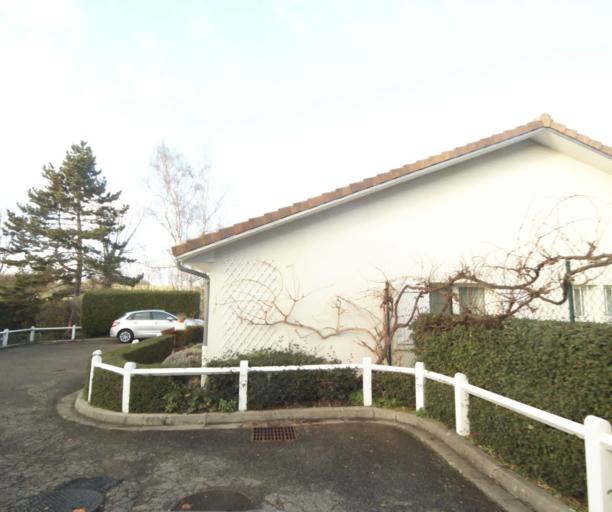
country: FR
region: Ile-de-France
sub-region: Departement des Yvelines
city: Meulan-en-Yvelines
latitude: 49.0144
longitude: 1.9159
